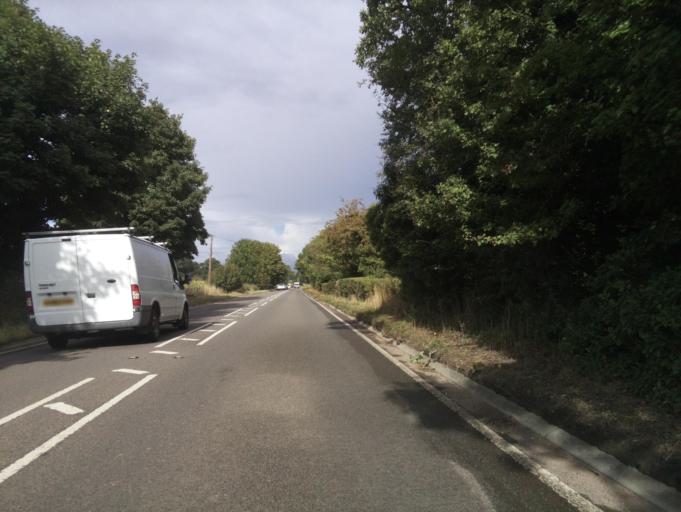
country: GB
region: England
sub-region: Telford and Wrekin
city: Madeley
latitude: 52.6501
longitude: -2.4018
